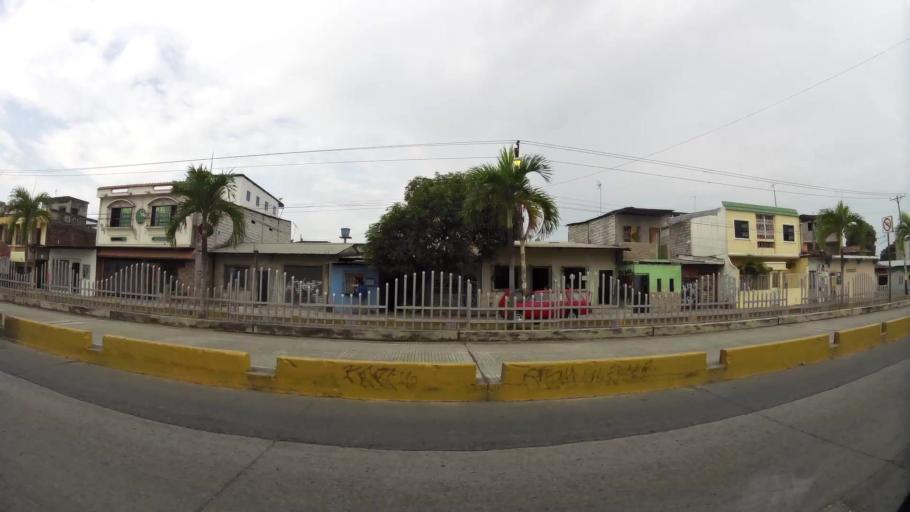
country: EC
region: Guayas
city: Guayaquil
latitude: -2.2581
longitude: -79.8792
